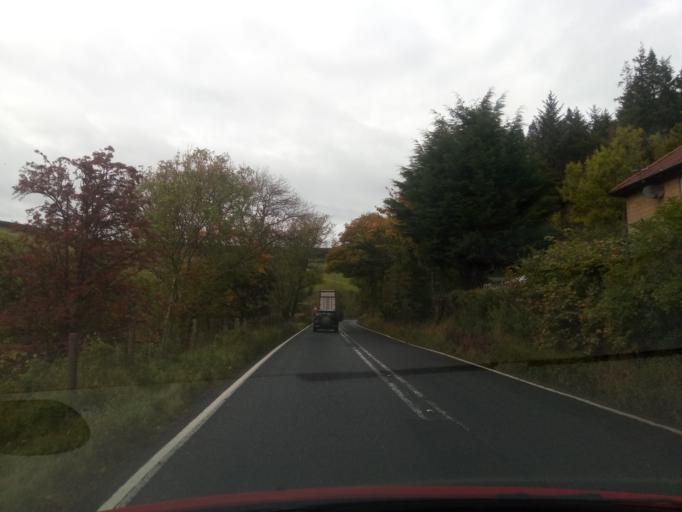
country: GB
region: Scotland
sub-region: The Scottish Borders
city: Galashiels
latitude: 55.7072
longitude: -2.8862
